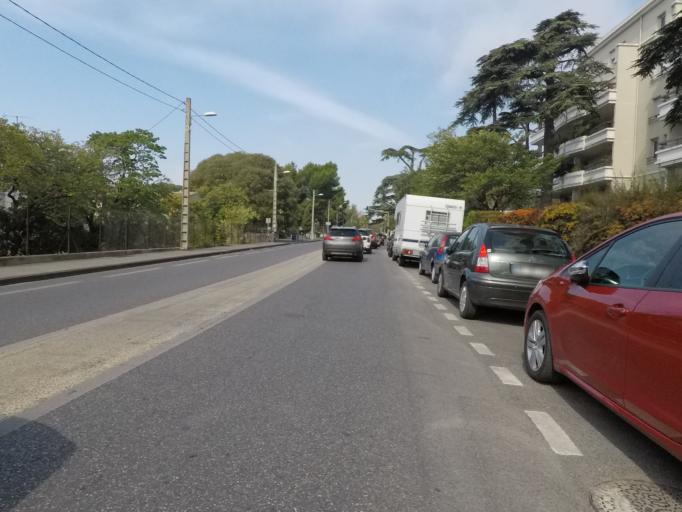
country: FR
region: Provence-Alpes-Cote d'Azur
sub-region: Departement des Bouches-du-Rhone
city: Marseille 09
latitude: 43.2533
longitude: 5.4218
